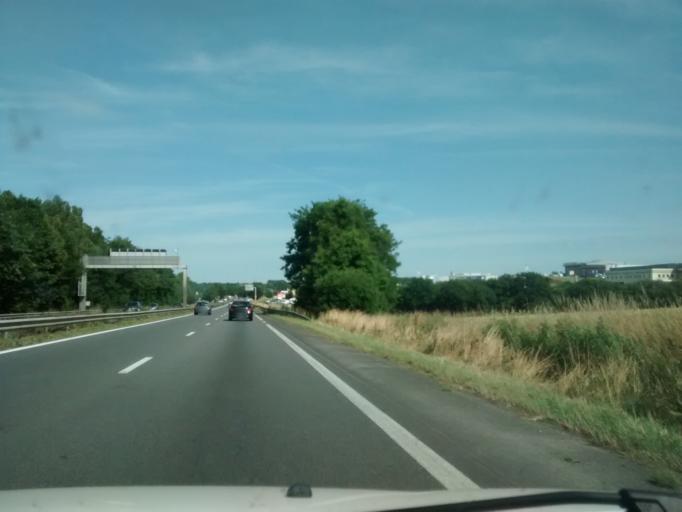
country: FR
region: Brittany
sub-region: Departement des Cotes-d'Armor
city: Yffiniac
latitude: 48.4812
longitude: -2.6806
